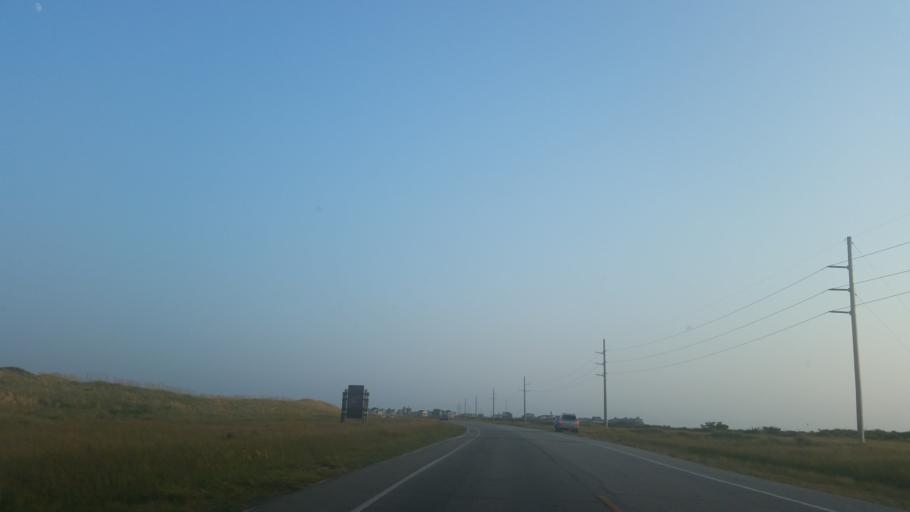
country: US
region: North Carolina
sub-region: Dare County
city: Wanchese
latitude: 35.6168
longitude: -75.4682
